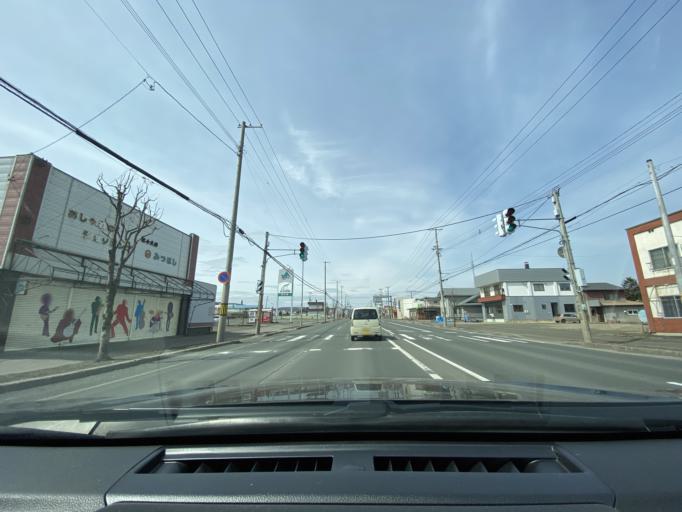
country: JP
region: Hokkaido
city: Kitami
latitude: 43.7974
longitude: 143.7570
